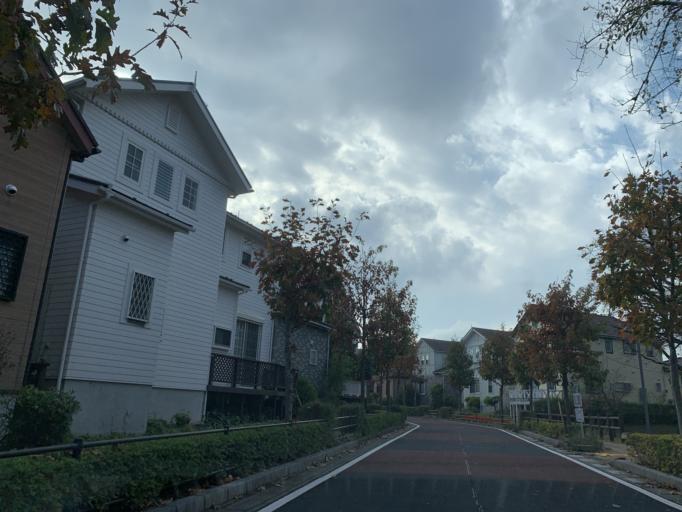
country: JP
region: Chiba
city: Nagareyama
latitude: 35.9116
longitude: 139.9141
